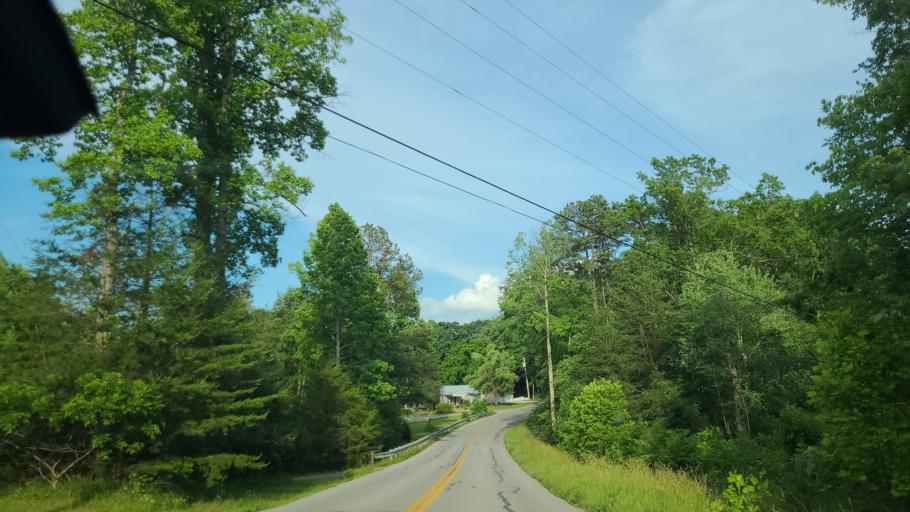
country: US
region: Kentucky
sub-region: Whitley County
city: Corbin
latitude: 36.9116
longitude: -84.2492
